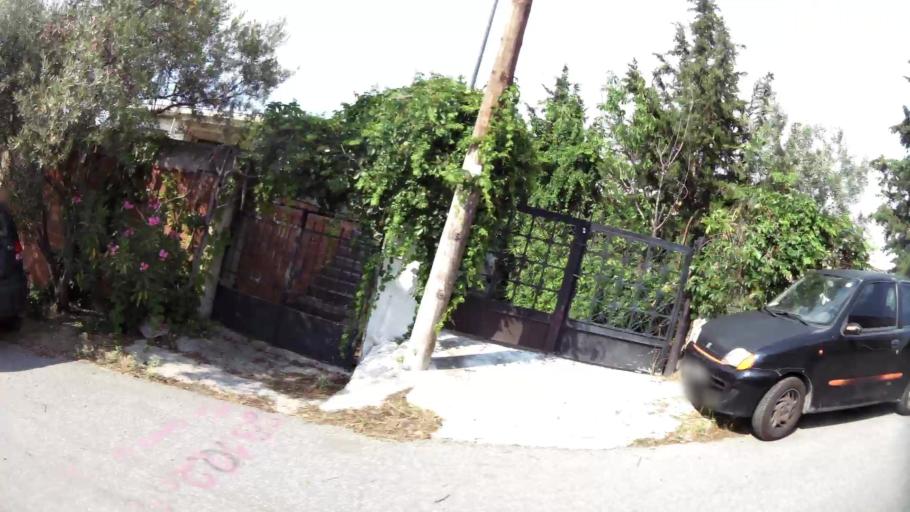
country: GR
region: Central Macedonia
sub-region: Nomos Thessalonikis
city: Polichni
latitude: 40.6619
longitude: 22.9665
